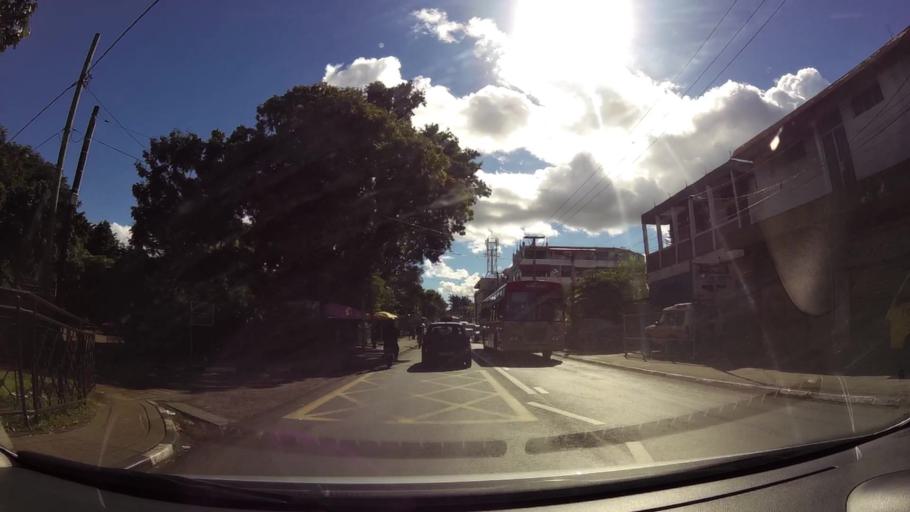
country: MU
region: Pamplemousses
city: Le Hochet
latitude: -20.1447
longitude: 57.5239
